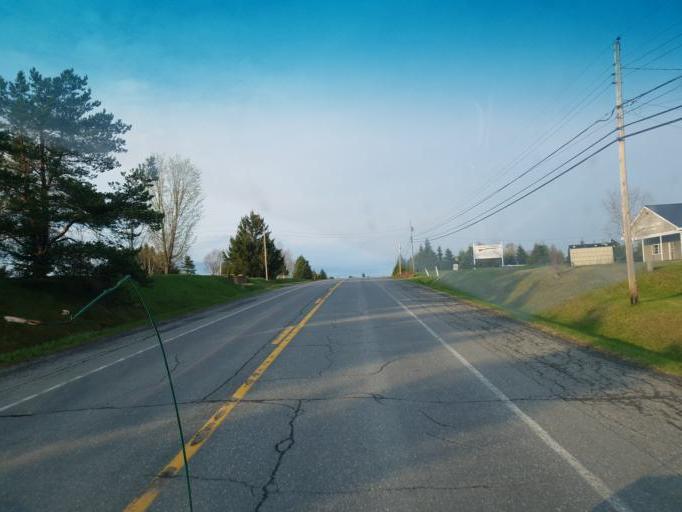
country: US
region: Maine
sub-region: Aroostook County
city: Caribou
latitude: 46.8518
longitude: -68.0357
